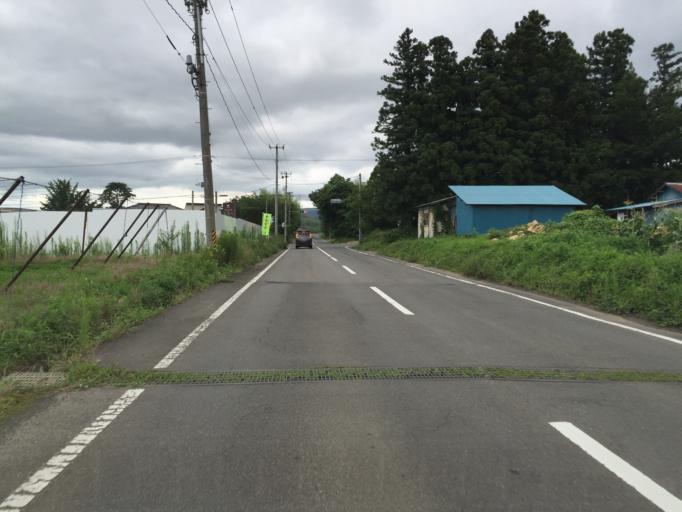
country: JP
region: Fukushima
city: Fukushima-shi
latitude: 37.7565
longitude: 140.3622
